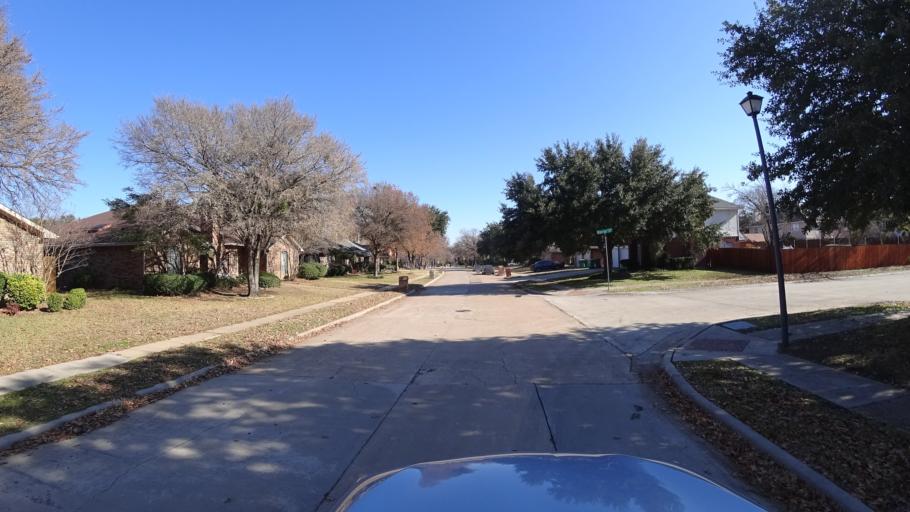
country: US
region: Texas
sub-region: Denton County
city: Lewisville
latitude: 33.0166
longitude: -97.0243
